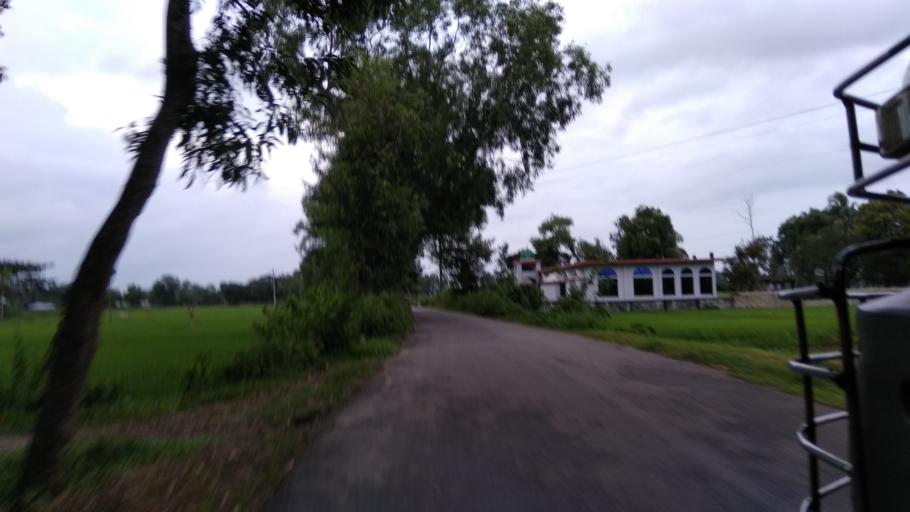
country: IN
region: Tripura
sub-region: Dhalai
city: Kamalpur
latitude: 24.2215
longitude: 91.8549
